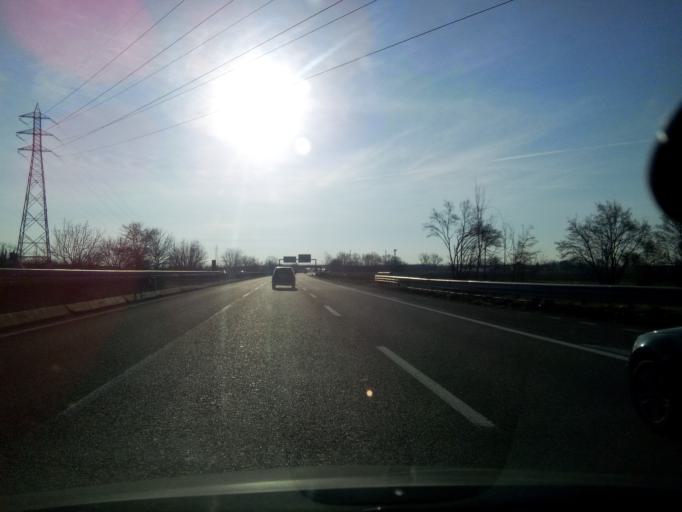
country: IT
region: Emilia-Romagna
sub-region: Provincia di Parma
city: Ponte Taro
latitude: 44.8680
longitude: 10.2204
